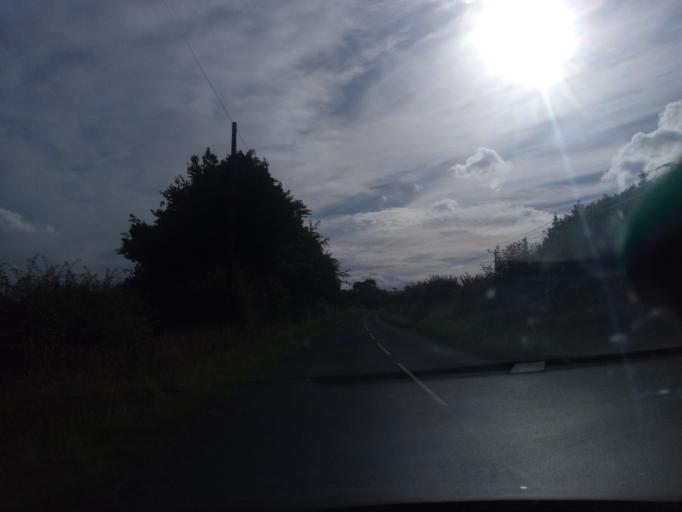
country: GB
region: Scotland
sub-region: The Scottish Borders
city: Coldstream
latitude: 55.5337
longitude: -2.2946
